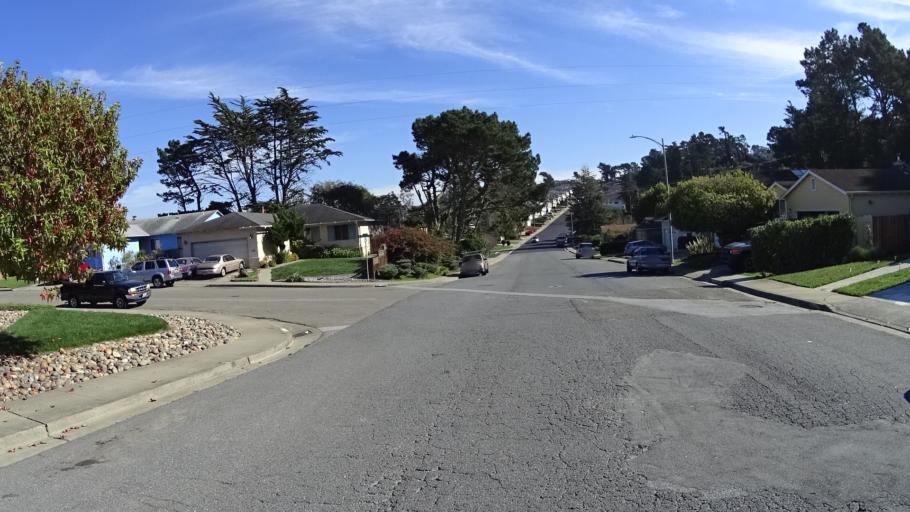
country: US
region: California
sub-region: San Mateo County
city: Pacifica
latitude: 37.6375
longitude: -122.4570
